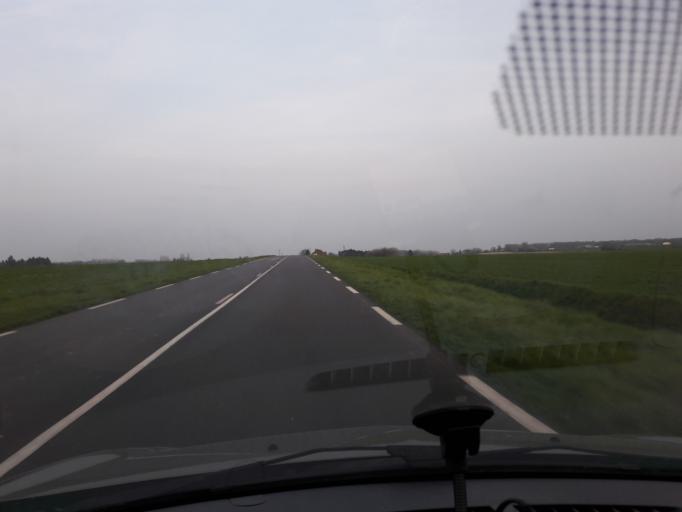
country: FR
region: Nord-Pas-de-Calais
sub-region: Departement du Nord
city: Recquignies
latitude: 50.2567
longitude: 4.0533
